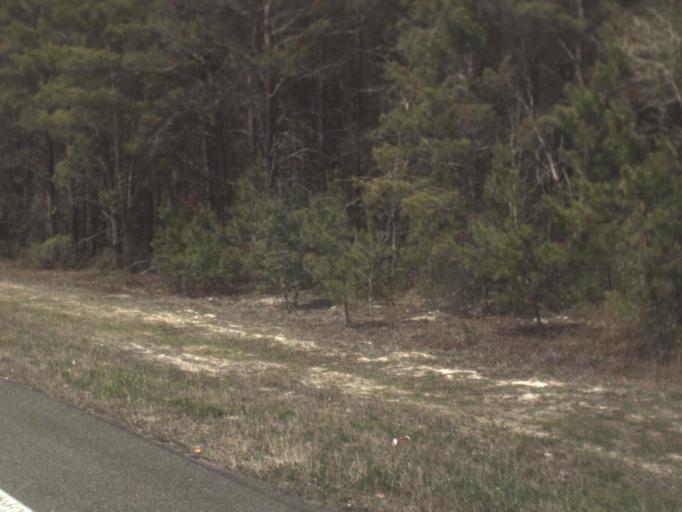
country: US
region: Florida
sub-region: Liberty County
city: Bristol
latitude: 30.5077
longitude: -84.8362
